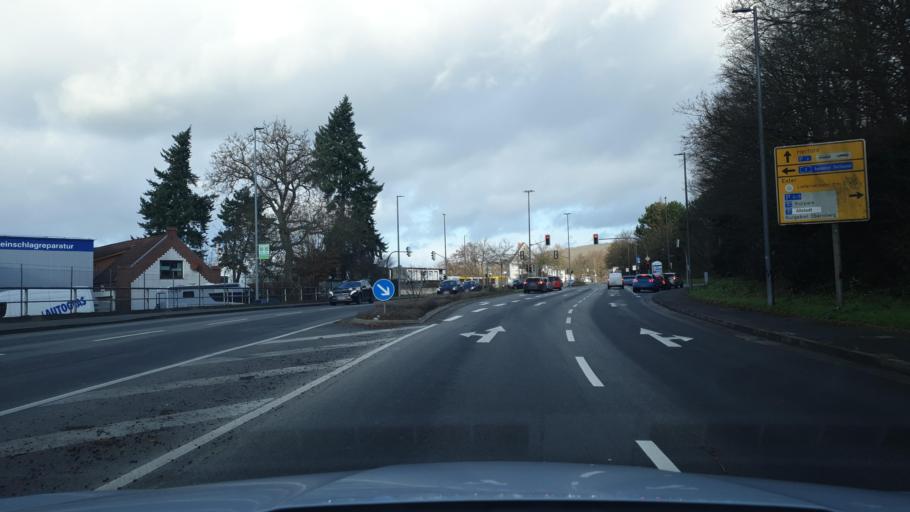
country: DE
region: North Rhine-Westphalia
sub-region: Regierungsbezirk Detmold
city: Bad Salzuflen
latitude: 52.0831
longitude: 8.7387
